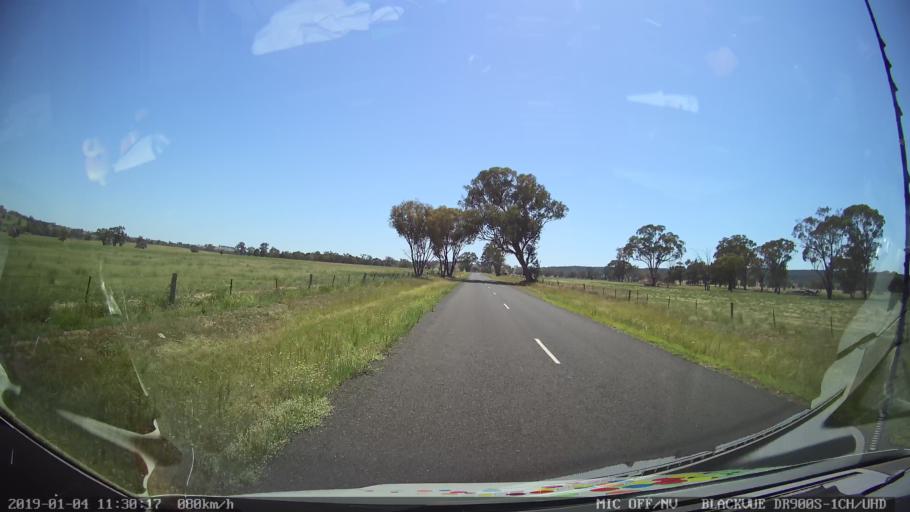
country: AU
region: New South Wales
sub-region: Cabonne
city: Molong
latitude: -33.0789
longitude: 148.7795
